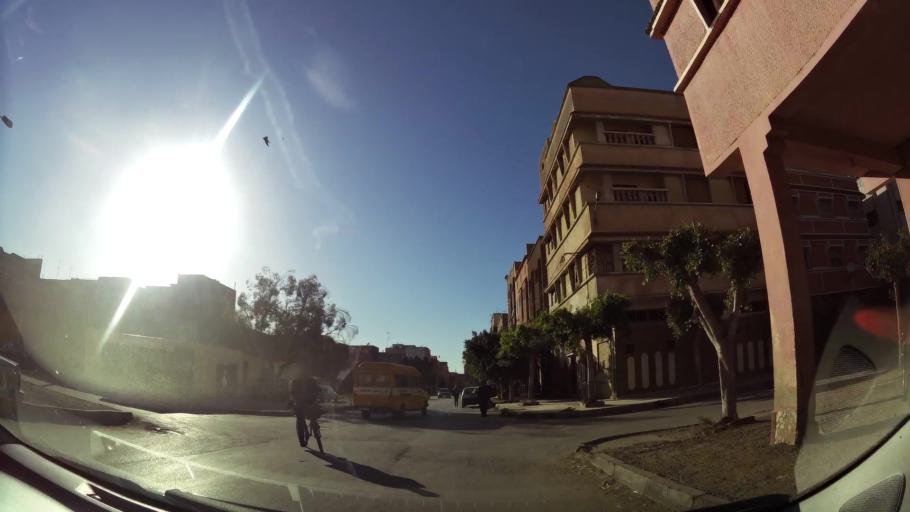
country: MA
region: Oriental
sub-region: Berkane-Taourirt
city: Berkane
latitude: 34.9252
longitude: -2.3381
